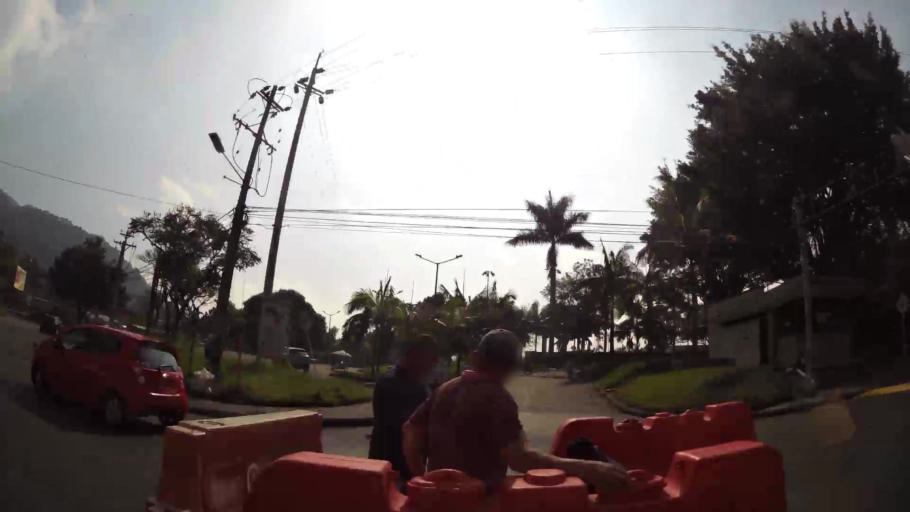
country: CO
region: Antioquia
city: La Estrella
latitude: 6.1706
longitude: -75.6281
